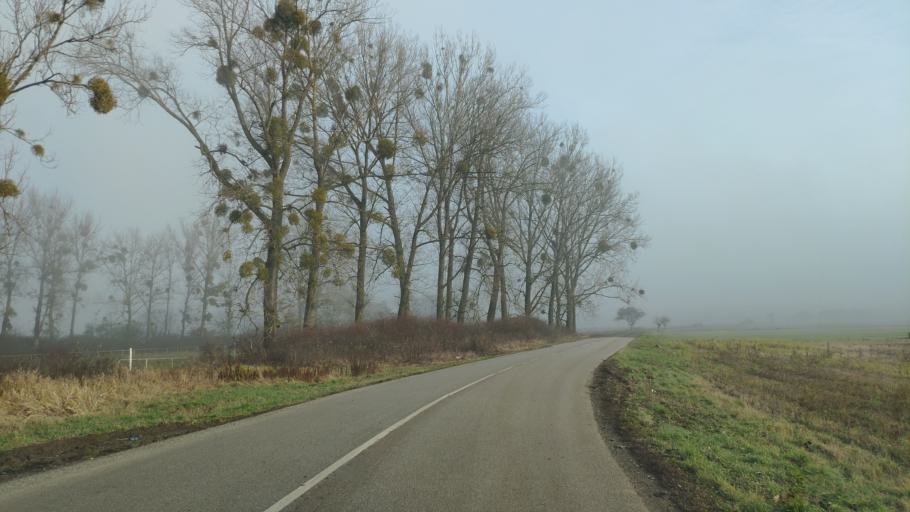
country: SK
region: Kosicky
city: Kosice
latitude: 48.7085
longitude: 21.4160
